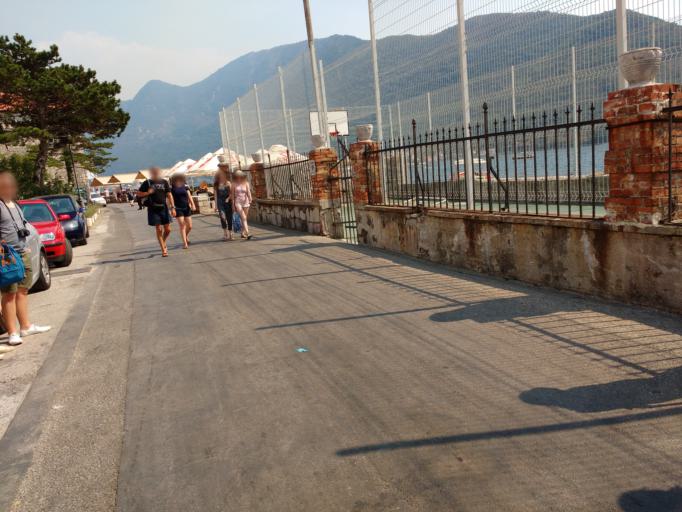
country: ME
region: Kotor
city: Risan
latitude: 42.4866
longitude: 18.6975
